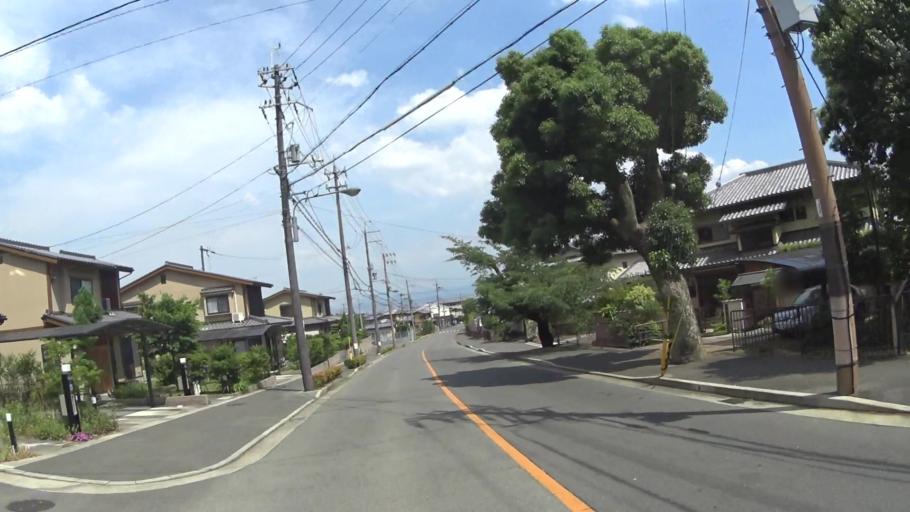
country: JP
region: Kyoto
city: Muko
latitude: 35.0263
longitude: 135.6716
